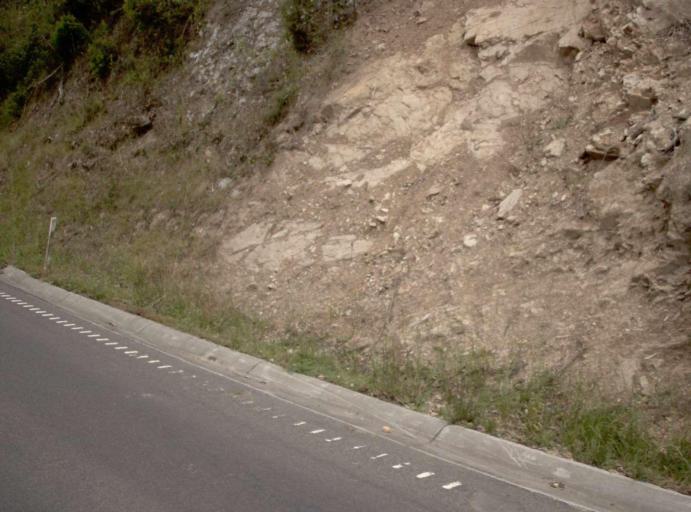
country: AU
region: Victoria
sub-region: Yarra Ranges
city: Yarra Glen
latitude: -37.5338
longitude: 145.4145
